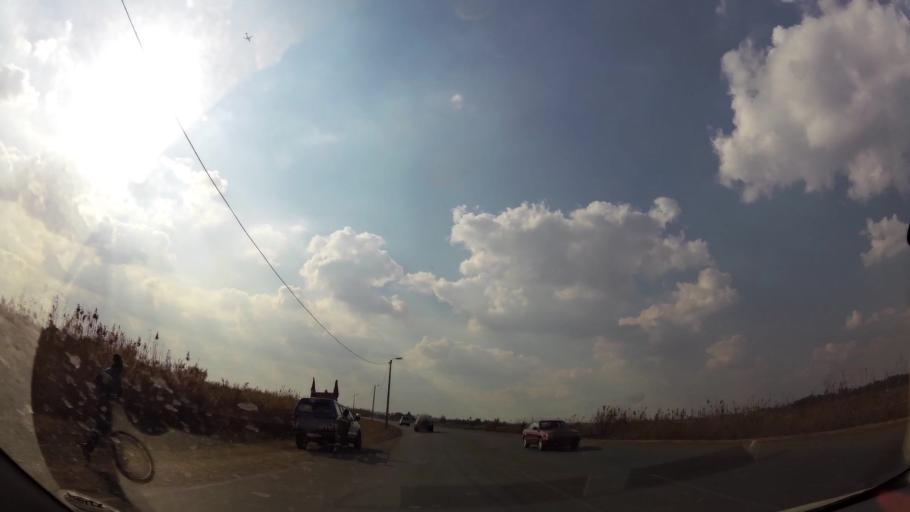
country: ZA
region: Gauteng
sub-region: Ekurhuleni Metropolitan Municipality
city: Germiston
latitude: -26.2991
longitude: 28.2133
